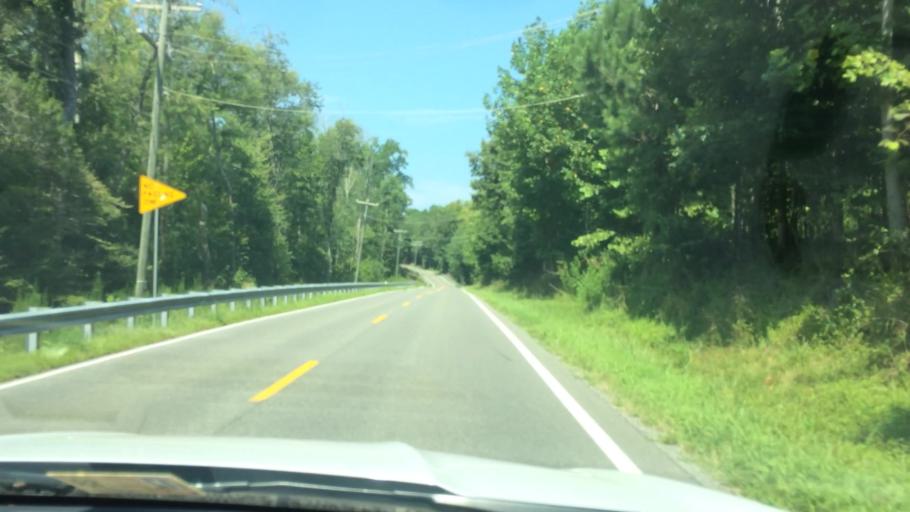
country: US
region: Virginia
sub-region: New Kent County
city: New Kent
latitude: 37.5273
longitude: -77.0826
